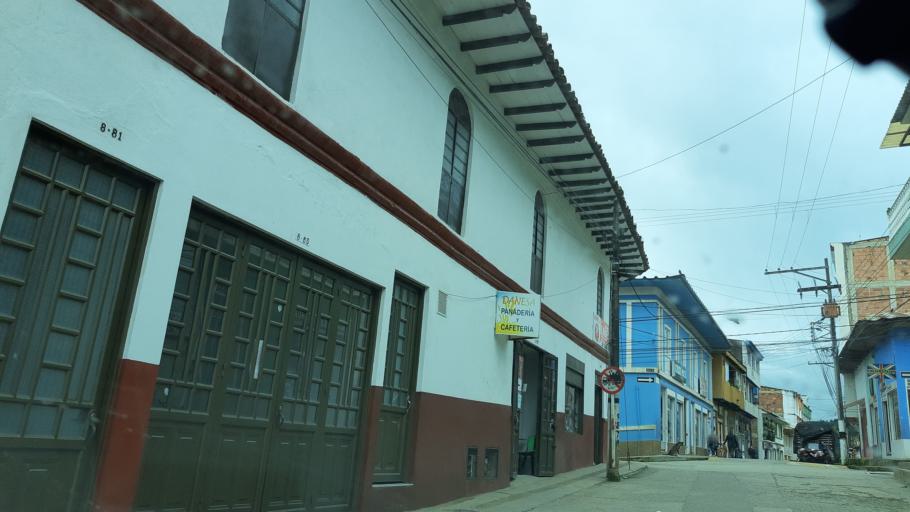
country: CO
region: Boyaca
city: Garagoa
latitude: 5.0803
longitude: -73.3637
